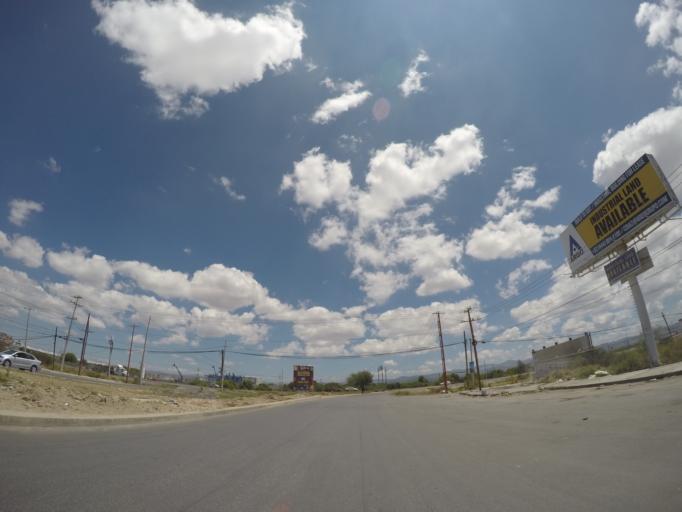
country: MX
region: San Luis Potosi
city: La Pila
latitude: 22.0524
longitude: -100.8625
